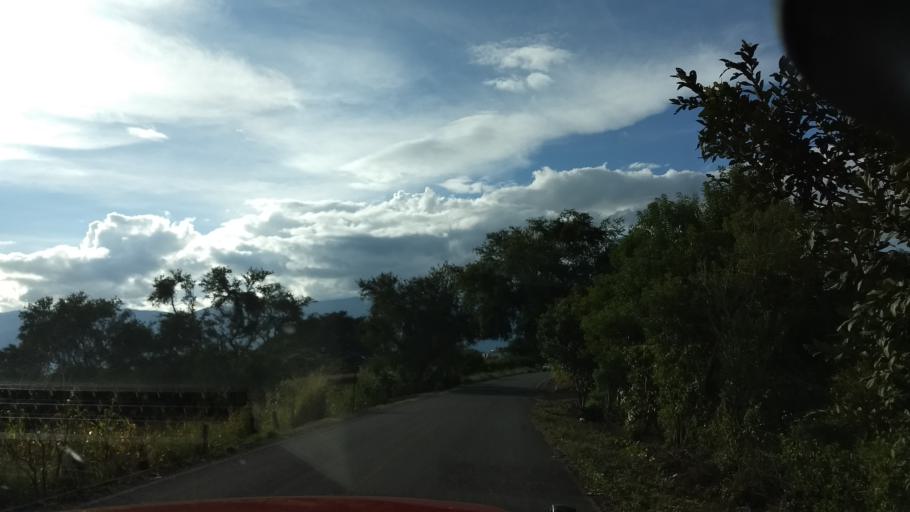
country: MX
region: Colima
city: Suchitlan
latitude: 19.4668
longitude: -103.7609
